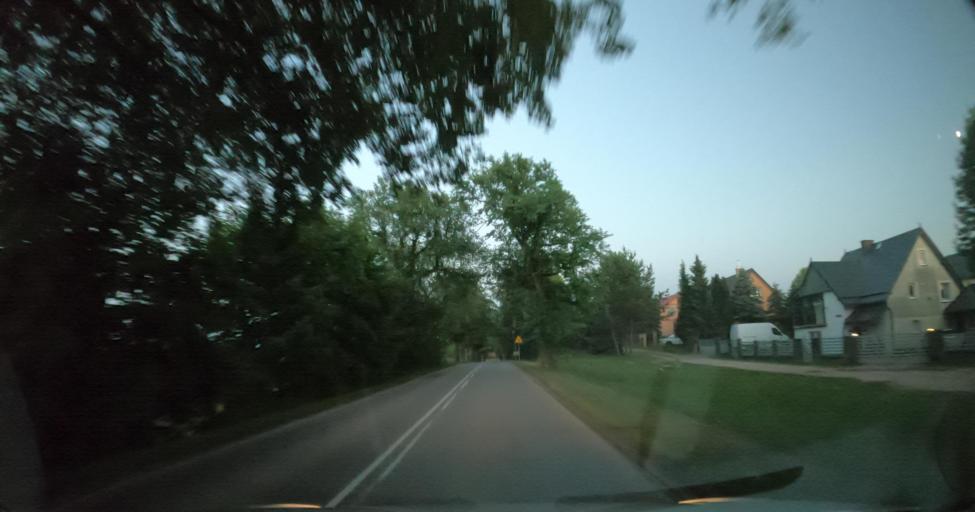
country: PL
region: Pomeranian Voivodeship
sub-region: Powiat wejherowski
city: Szemud
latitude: 54.4735
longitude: 18.2725
